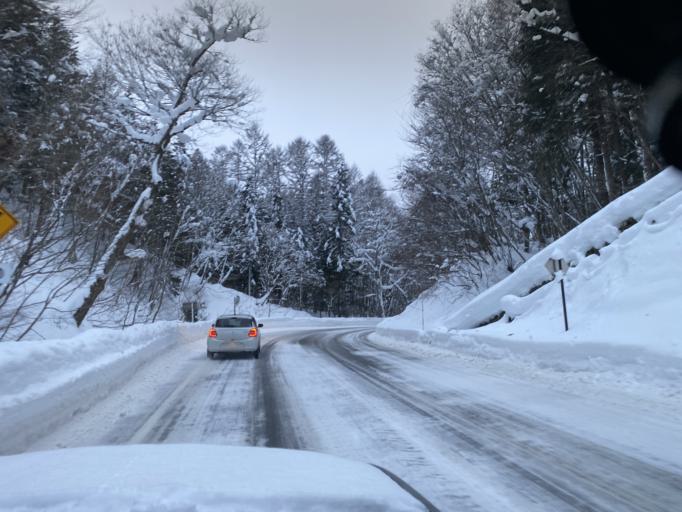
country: JP
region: Nagano
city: Omachi
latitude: 36.5801
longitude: 137.8812
